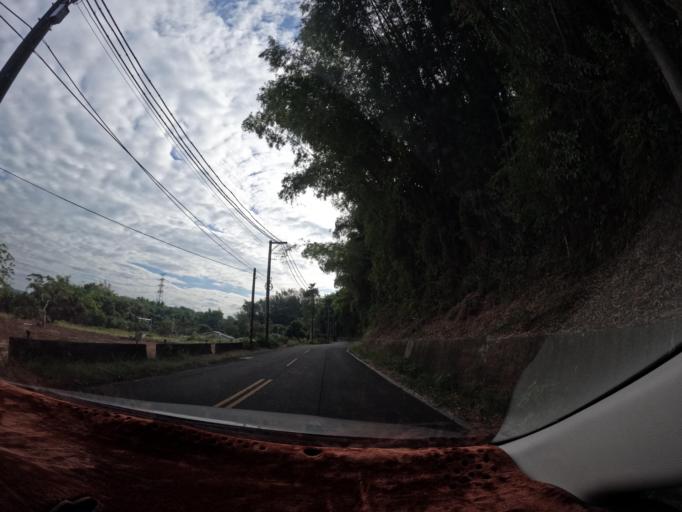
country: TW
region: Taiwan
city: Yujing
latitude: 23.0239
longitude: 120.4118
